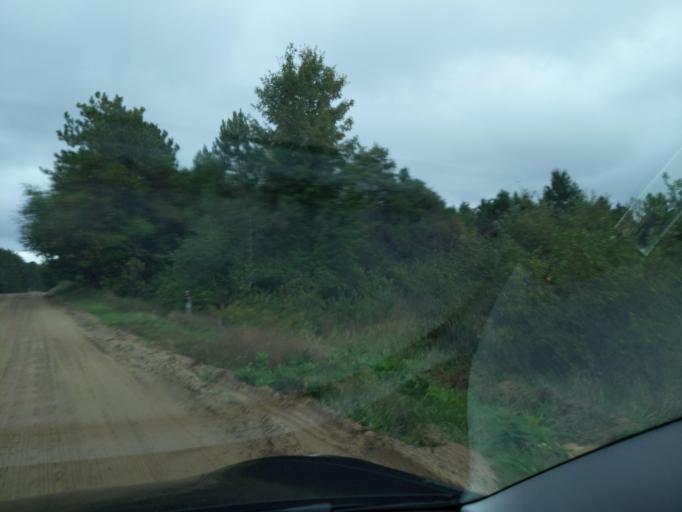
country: US
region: Michigan
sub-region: Antrim County
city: Elk Rapids
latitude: 44.8164
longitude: -85.3919
